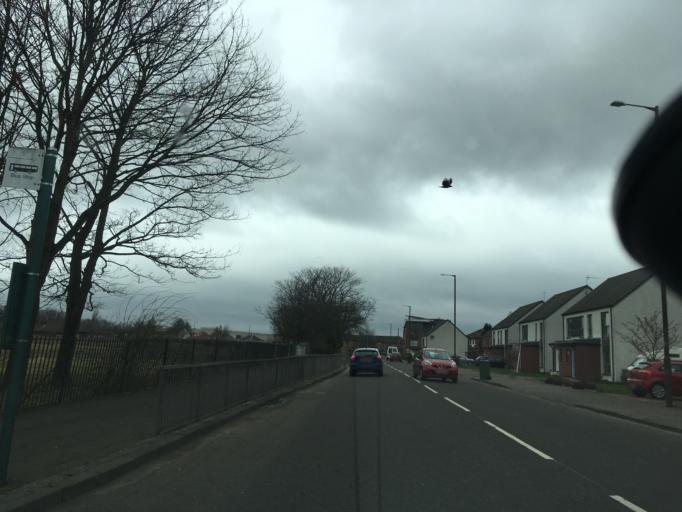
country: GB
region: Scotland
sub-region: Stirling
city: Stirling
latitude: 56.1294
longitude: -3.9558
